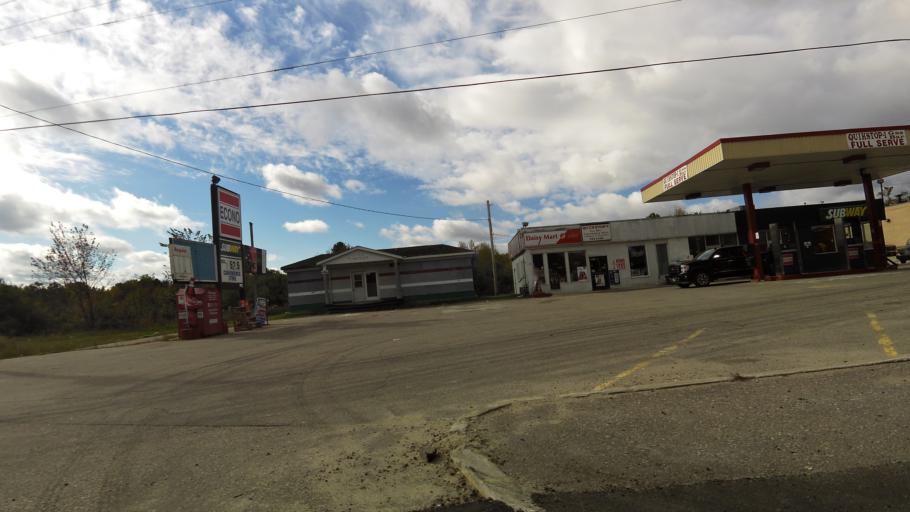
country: CA
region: Ontario
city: Deep River
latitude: 46.0973
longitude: -77.4933
